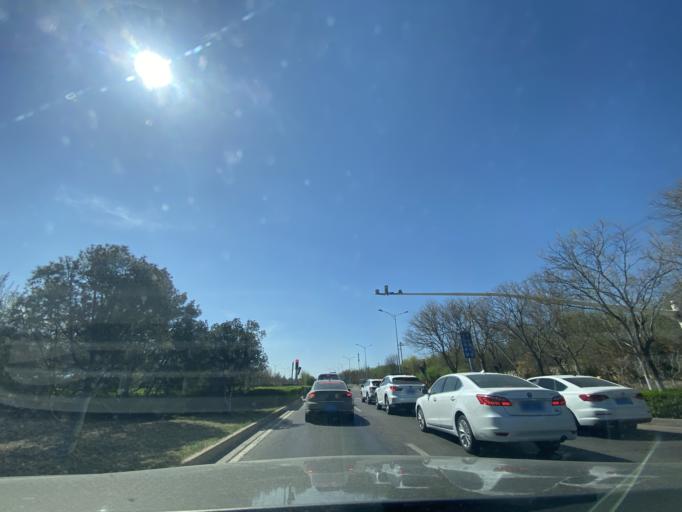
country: CN
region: Beijing
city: Sijiqing
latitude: 39.9426
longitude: 116.2406
